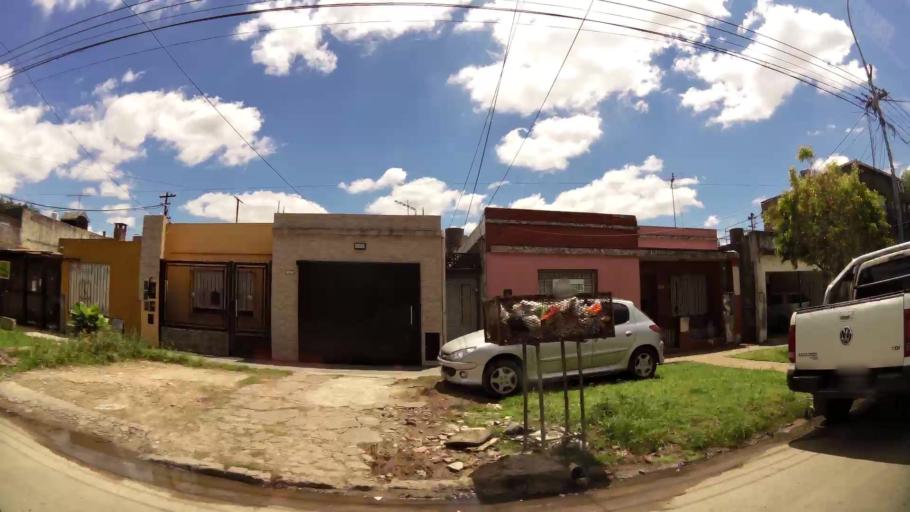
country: AR
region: Buenos Aires
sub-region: Partido de Lanus
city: Lanus
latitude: -34.7240
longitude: -58.4181
